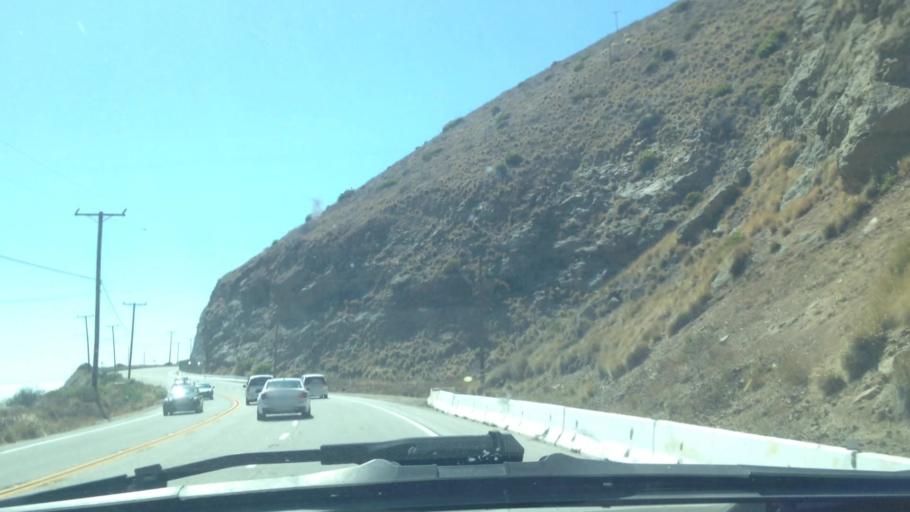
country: US
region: California
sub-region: Ventura County
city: Casa Conejo
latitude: 34.0668
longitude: -118.9991
